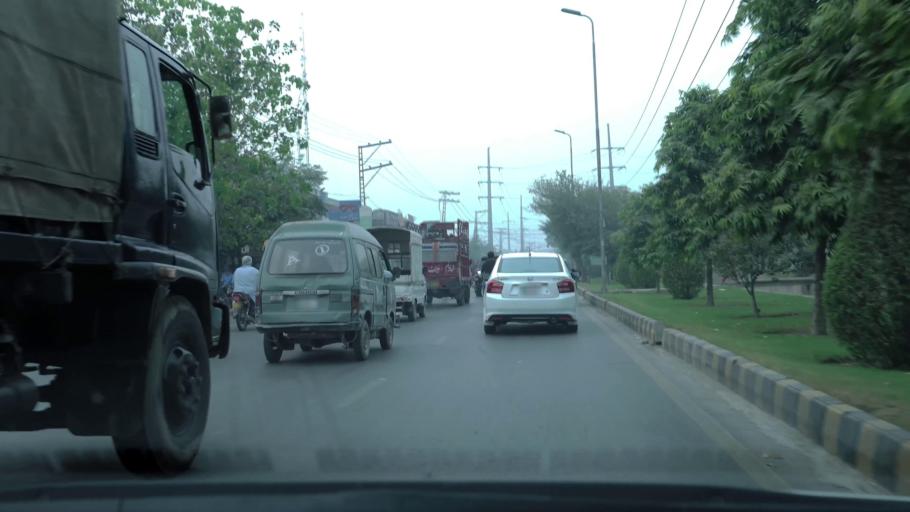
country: PK
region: Punjab
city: Lahore
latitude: 31.4783
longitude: 74.3008
